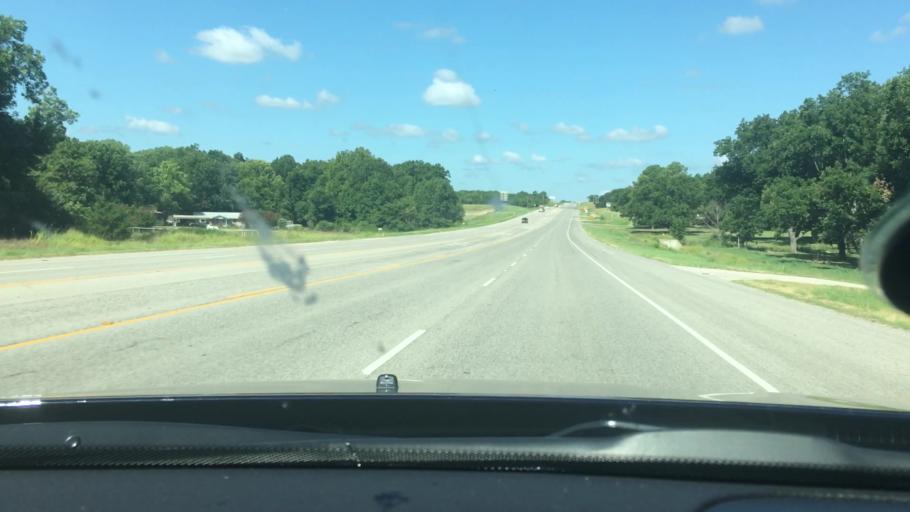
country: US
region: Oklahoma
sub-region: Marshall County
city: Oakland
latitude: 34.1001
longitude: -96.8031
